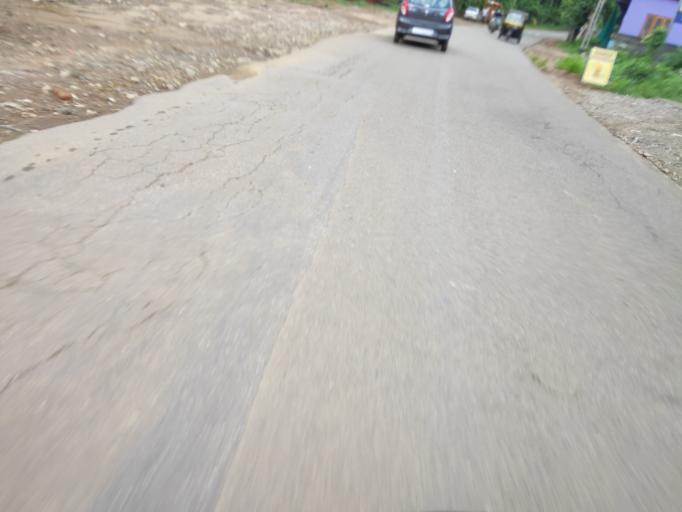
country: IN
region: Kerala
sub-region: Malappuram
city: Manjeri
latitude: 11.1976
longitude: 76.2240
